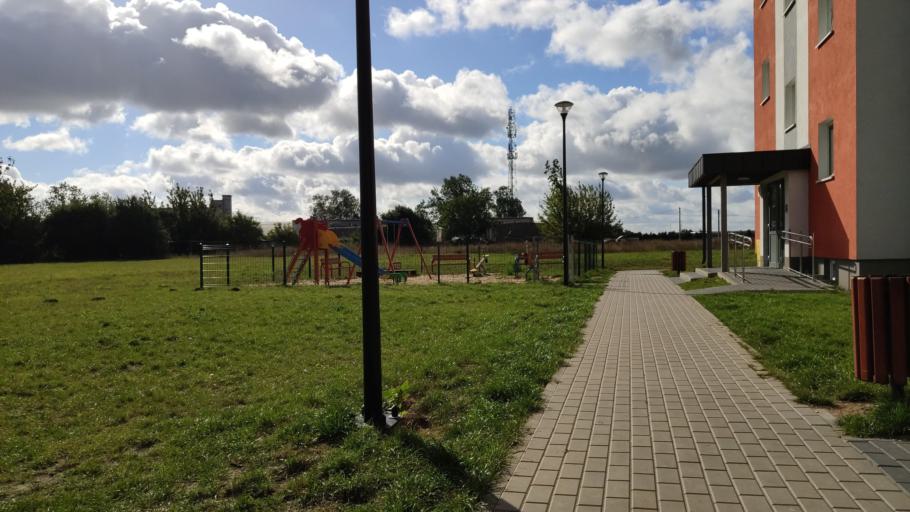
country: PL
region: Kujawsko-Pomorskie
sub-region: Powiat zninski
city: Znin
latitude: 52.8570
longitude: 17.7573
